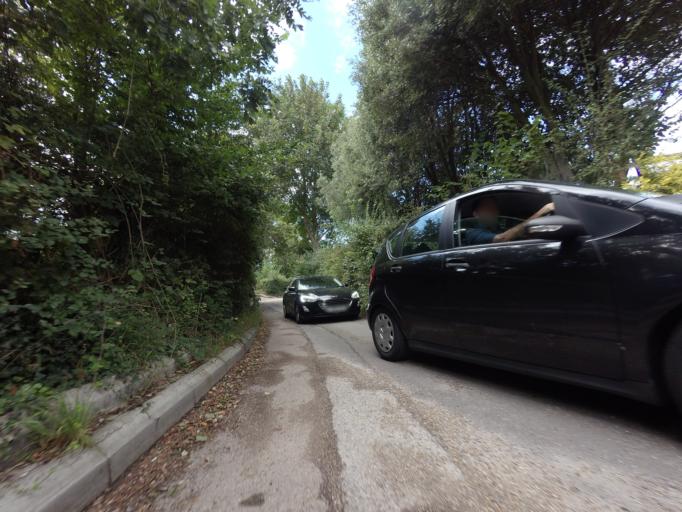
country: GB
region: England
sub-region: Kent
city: Shoreham
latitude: 51.3049
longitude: 0.1793
